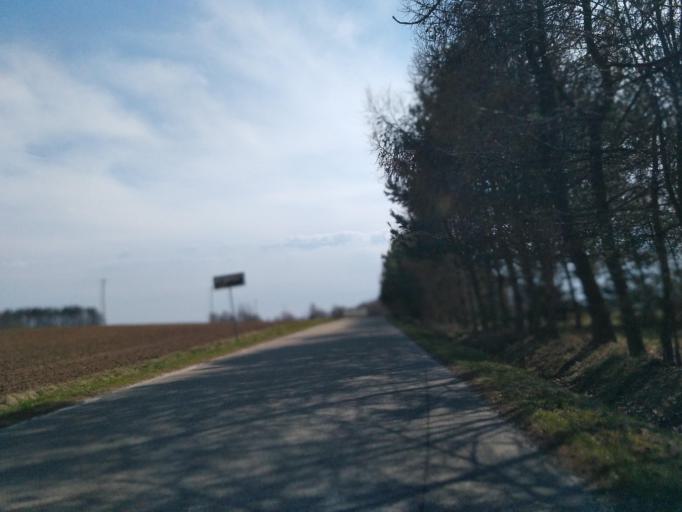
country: PL
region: Subcarpathian Voivodeship
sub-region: Powiat ropczycko-sedziszowski
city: Iwierzyce
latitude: 49.9758
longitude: 21.7473
